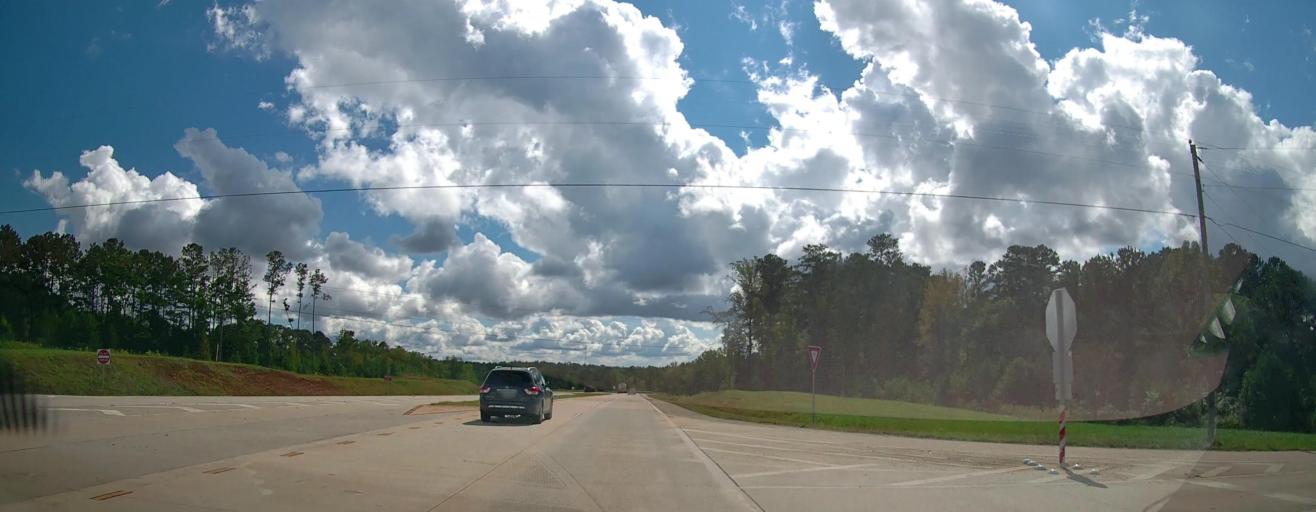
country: US
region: Georgia
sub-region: Jones County
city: Gray
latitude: 32.9971
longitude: -83.5741
